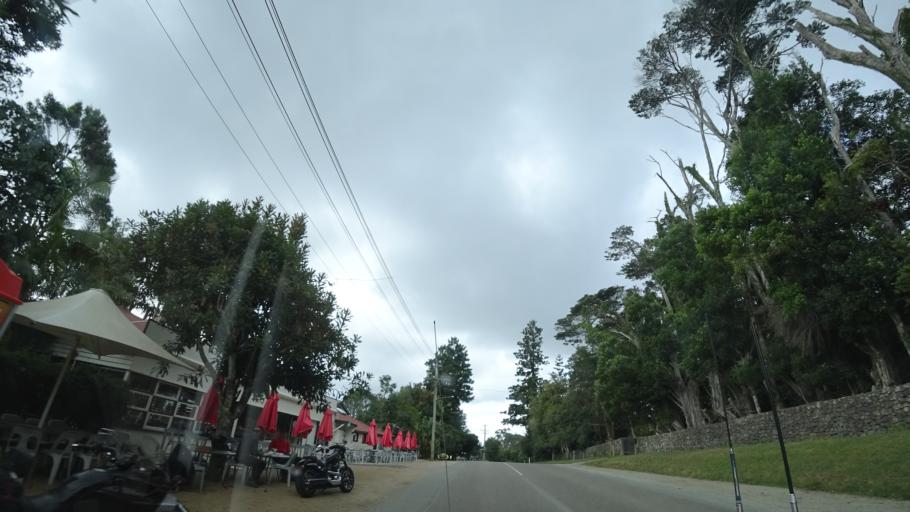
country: AU
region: Queensland
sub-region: Moreton Bay
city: Highvale
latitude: -27.3343
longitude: 152.7685
